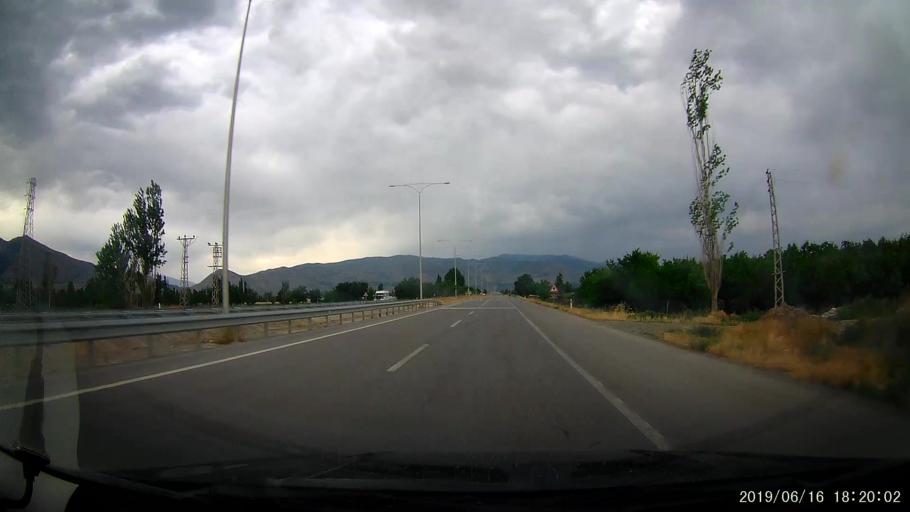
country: TR
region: Erzincan
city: Erzincan
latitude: 39.7191
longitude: 39.4788
